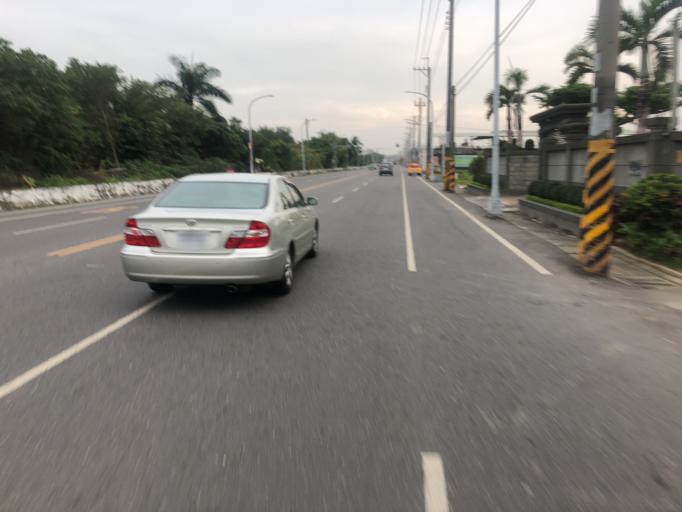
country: TW
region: Taiwan
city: Xinying
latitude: 23.1469
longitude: 120.2880
